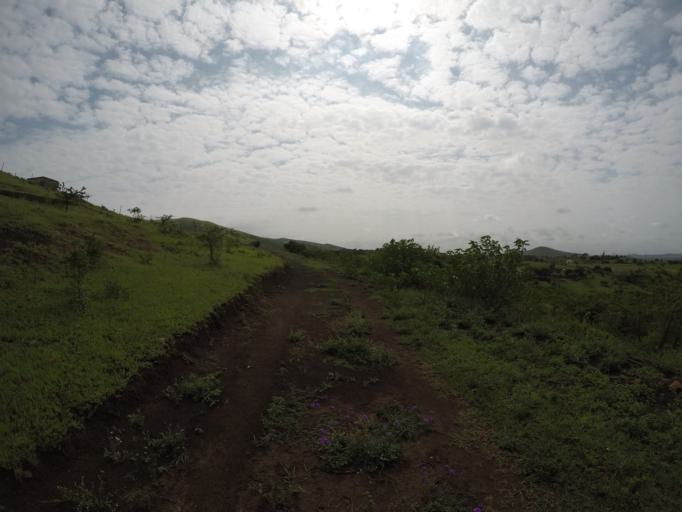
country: ZA
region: KwaZulu-Natal
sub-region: uThungulu District Municipality
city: Empangeni
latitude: -28.6176
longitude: 31.8993
